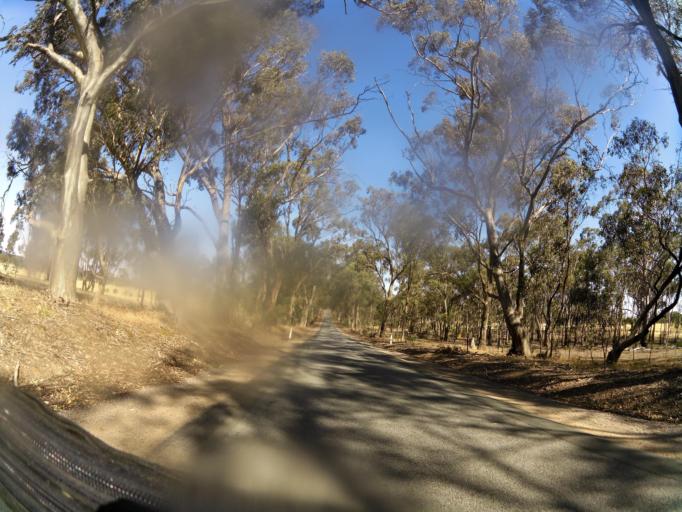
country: AU
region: Victoria
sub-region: Campaspe
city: Kyabram
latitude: -36.8792
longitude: 145.0889
